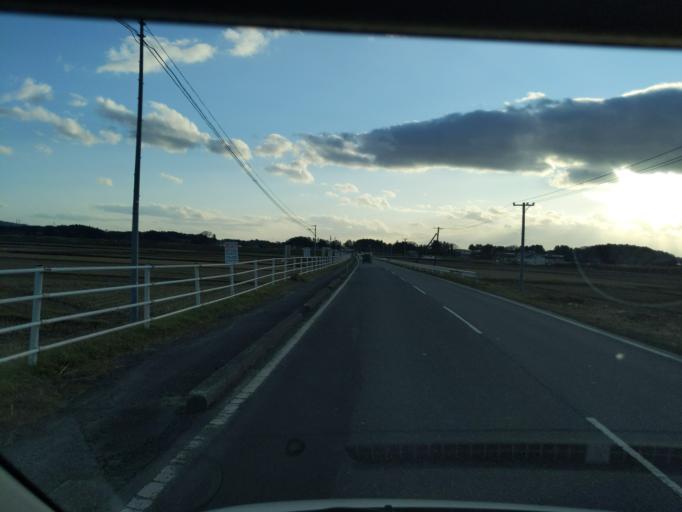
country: JP
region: Miyagi
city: Kogota
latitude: 38.6424
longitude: 141.0730
